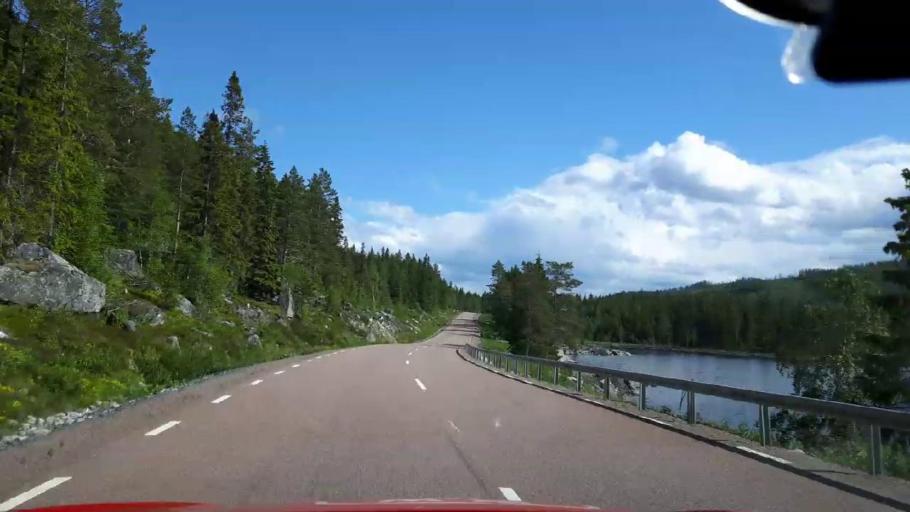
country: SE
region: Jaemtland
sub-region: Krokoms Kommun
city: Valla
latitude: 64.0241
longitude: 14.2011
